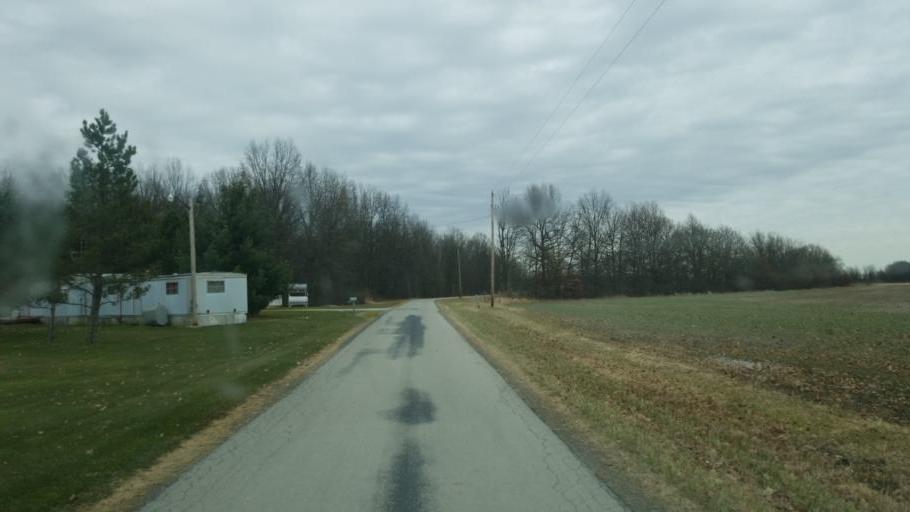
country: US
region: Ohio
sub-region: Wyandot County
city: Upper Sandusky
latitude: 40.7214
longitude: -83.3525
